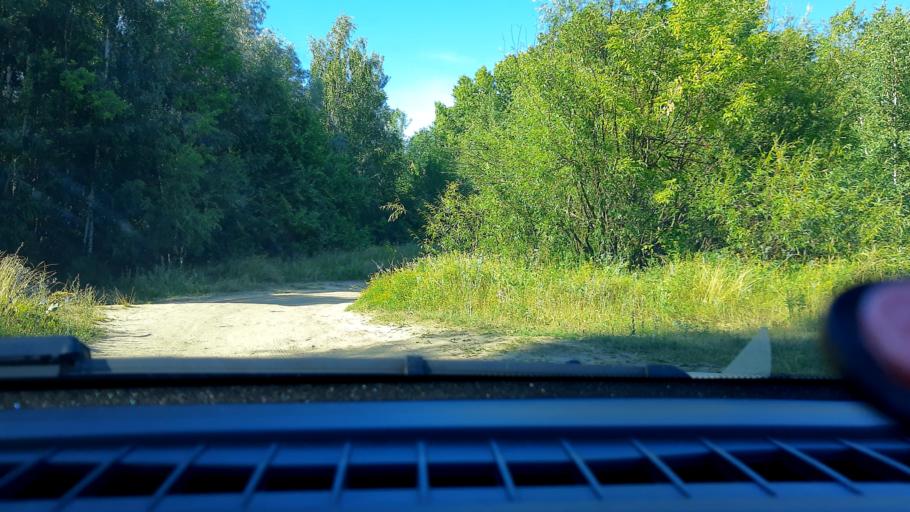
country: RU
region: Nizjnij Novgorod
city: Burevestnik
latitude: 56.1983
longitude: 43.8204
